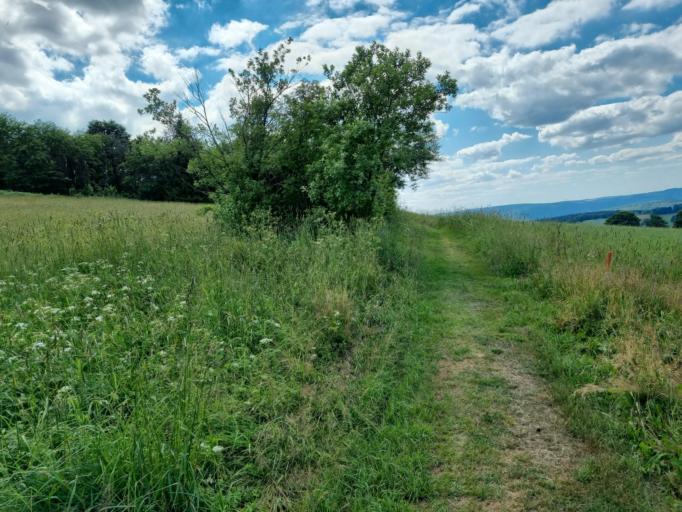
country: DE
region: Saxony
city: Deutschneudorf
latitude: 50.6349
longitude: 13.4679
